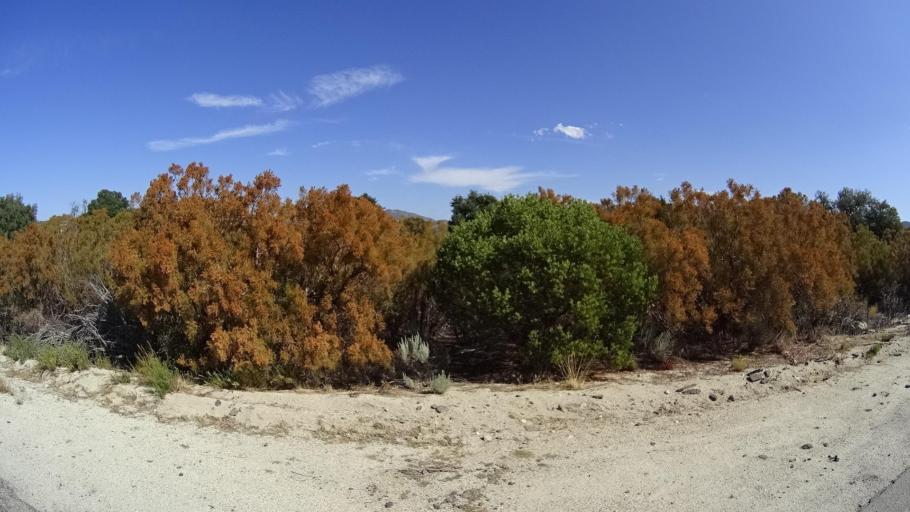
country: US
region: California
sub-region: Riverside County
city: Anza
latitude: 33.3845
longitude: -116.6899
